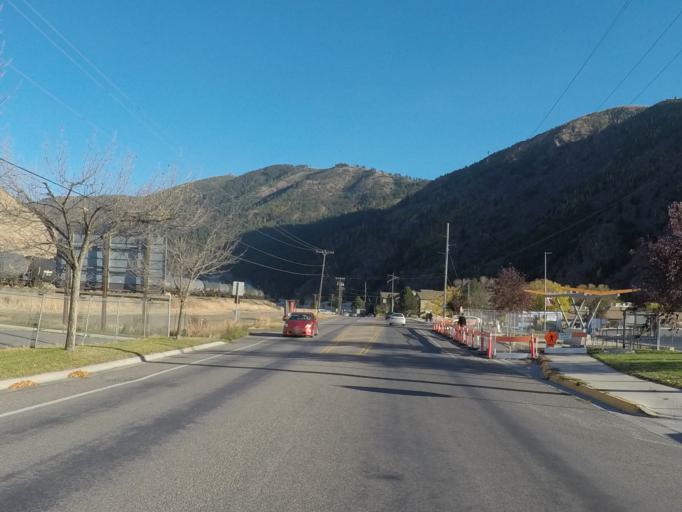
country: US
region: Montana
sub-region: Missoula County
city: Missoula
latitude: 46.8655
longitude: -113.9754
